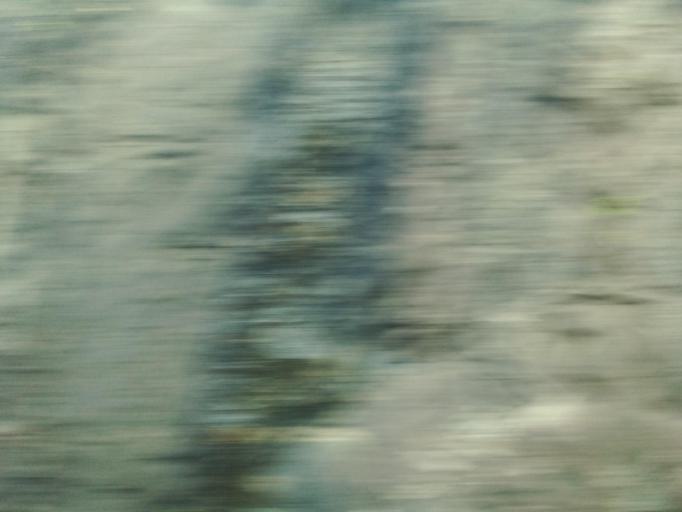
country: BR
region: Minas Gerais
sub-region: Nova Era
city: Nova Era
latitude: -19.7208
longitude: -42.9663
